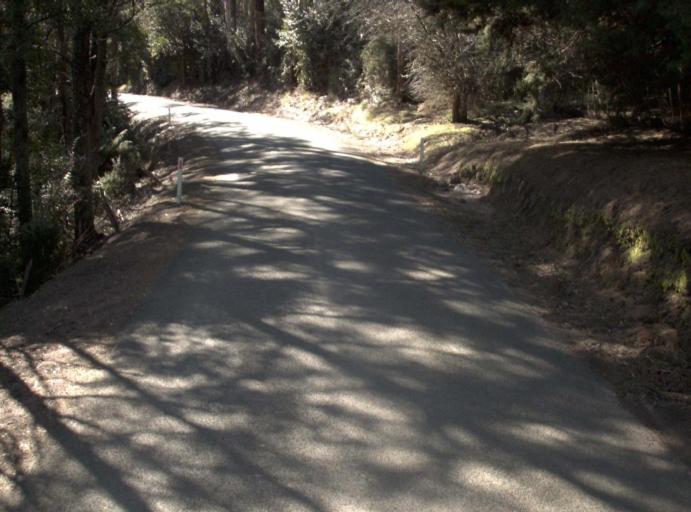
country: AU
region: Tasmania
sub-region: Launceston
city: Mayfield
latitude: -41.3010
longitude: 147.2003
